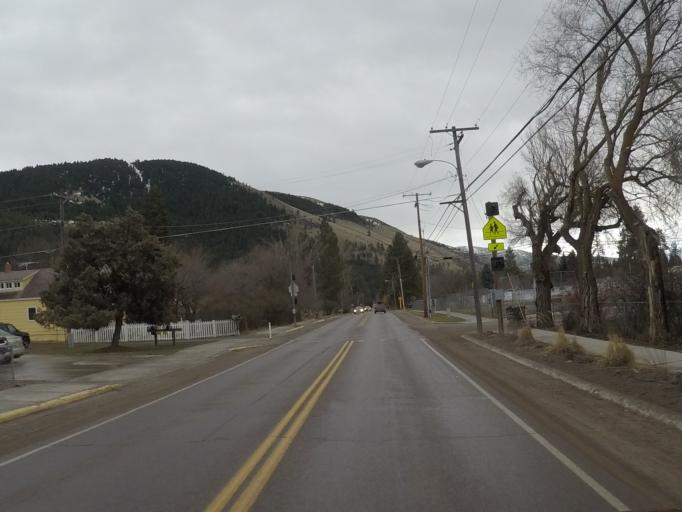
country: US
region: Montana
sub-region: Missoula County
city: East Missoula
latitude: 46.8928
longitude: -113.9657
